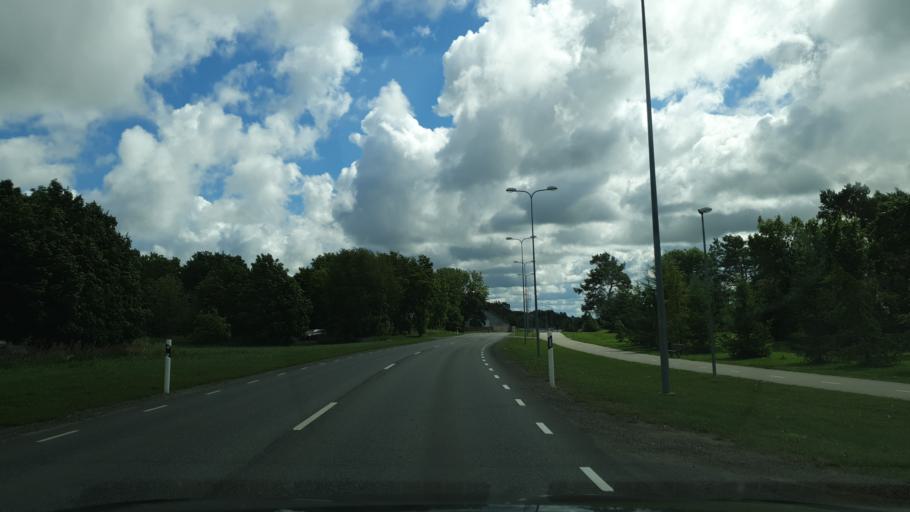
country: EE
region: Harju
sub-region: Viimsi vald
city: Viimsi
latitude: 59.5078
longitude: 24.8598
